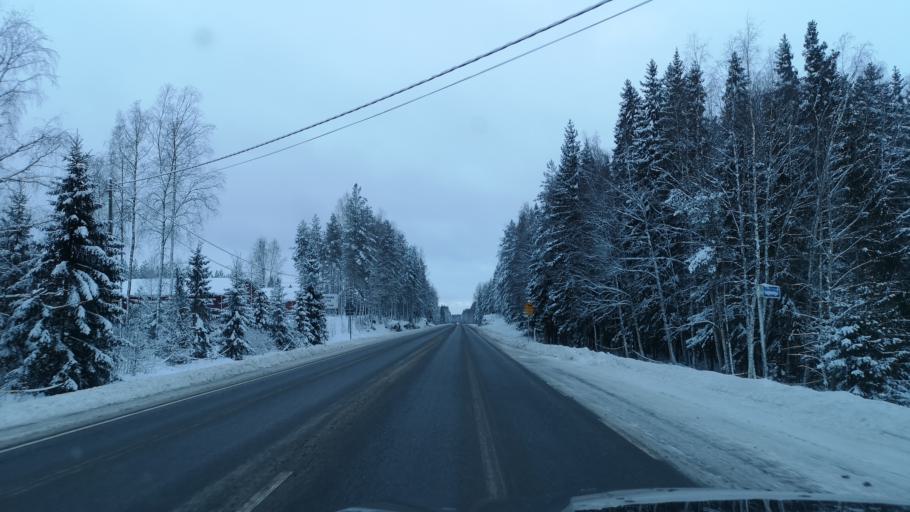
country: FI
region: Varsinais-Suomi
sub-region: Loimaa
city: Loimaa
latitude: 60.9150
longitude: 23.1856
